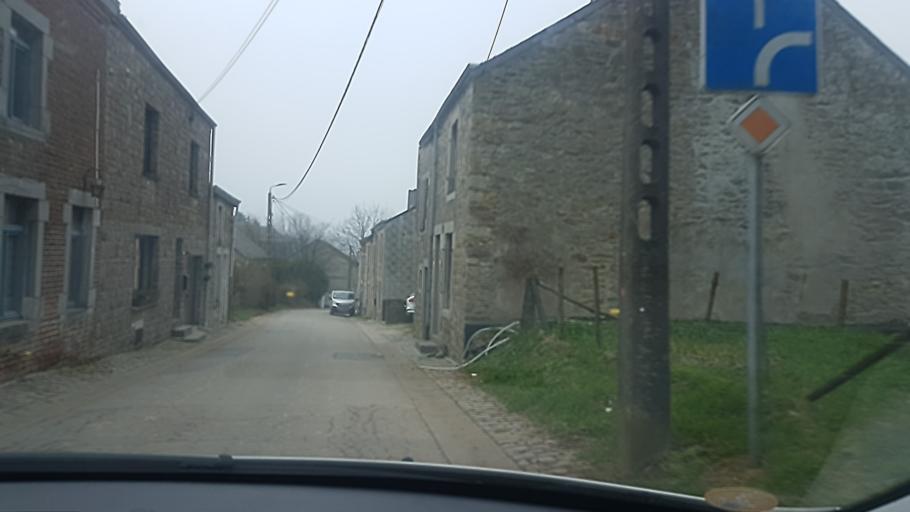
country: FR
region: Champagne-Ardenne
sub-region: Departement des Ardennes
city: Haybes
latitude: 50.0323
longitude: 4.6714
